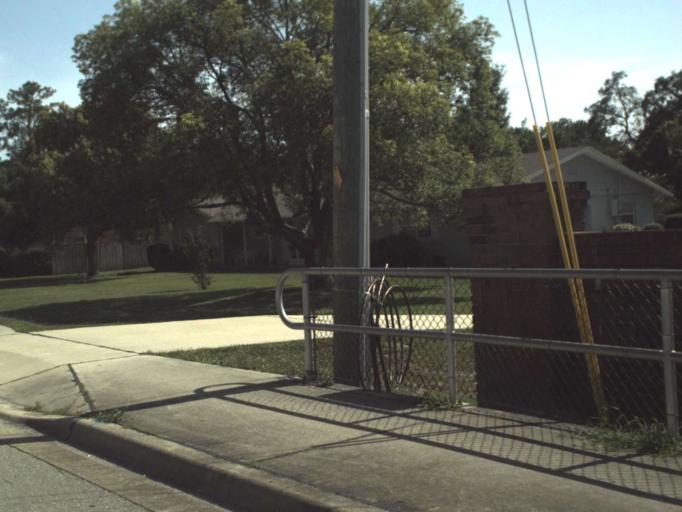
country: US
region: Florida
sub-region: Seminole County
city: Oviedo
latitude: 28.6384
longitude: -81.2082
